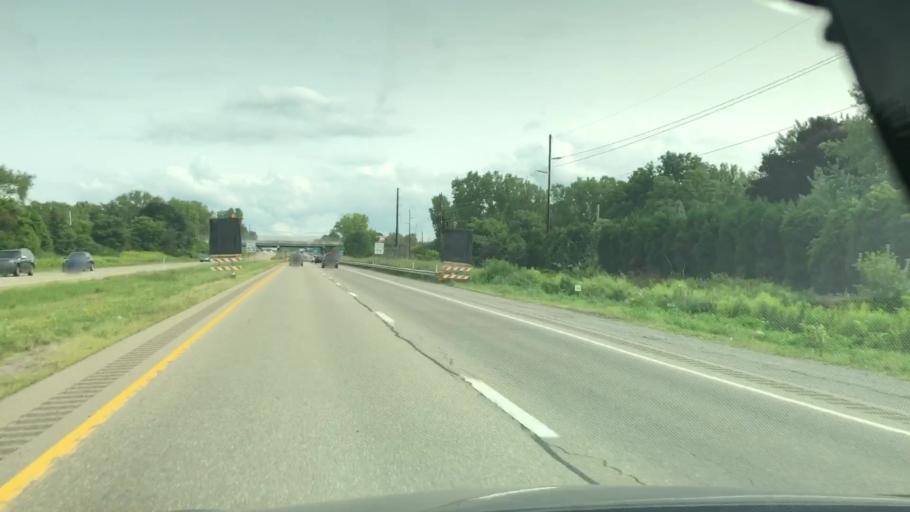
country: US
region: Pennsylvania
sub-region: Erie County
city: Erie
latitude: 42.0868
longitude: -80.1171
